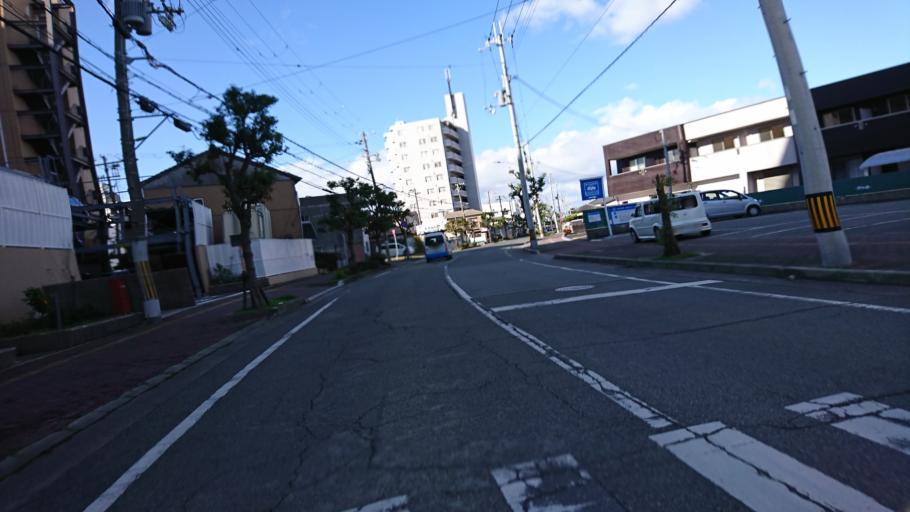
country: JP
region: Hyogo
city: Kakogawacho-honmachi
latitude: 34.7531
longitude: 134.8029
